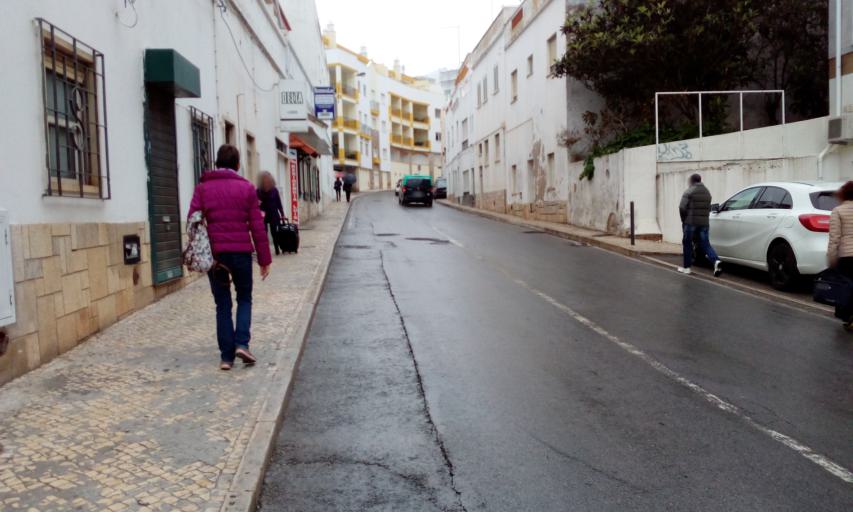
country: PT
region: Faro
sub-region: Albufeira
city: Albufeira
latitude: 37.0905
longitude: -8.2497
